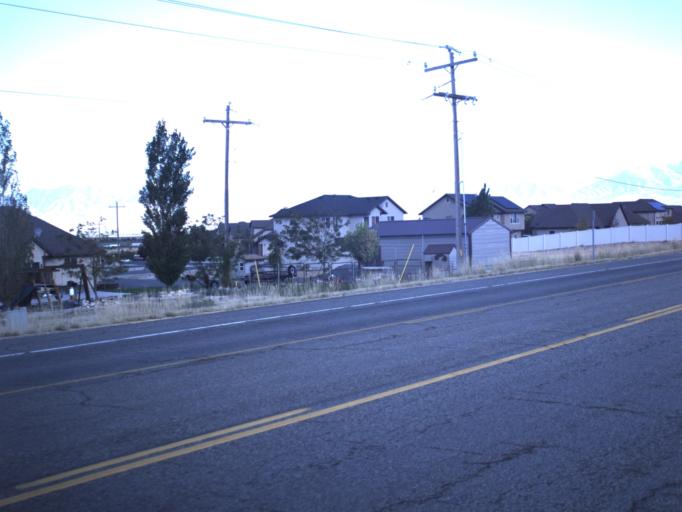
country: US
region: Utah
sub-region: Tooele County
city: Grantsville
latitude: 40.6214
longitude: -112.5041
